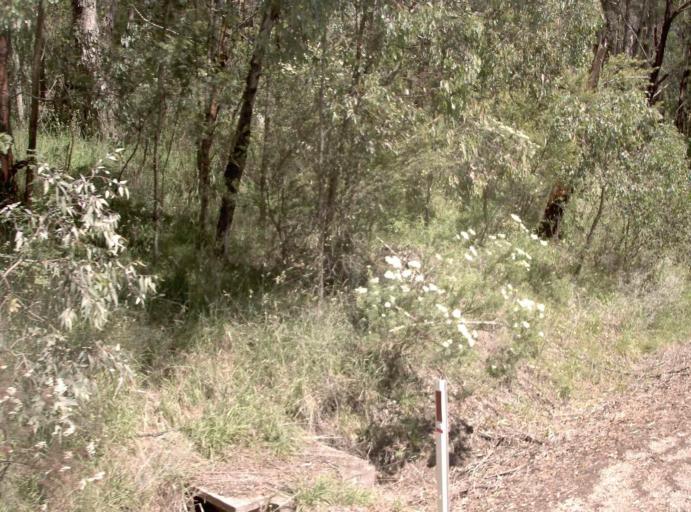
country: AU
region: Victoria
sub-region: East Gippsland
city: Lakes Entrance
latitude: -37.3434
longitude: 148.2297
